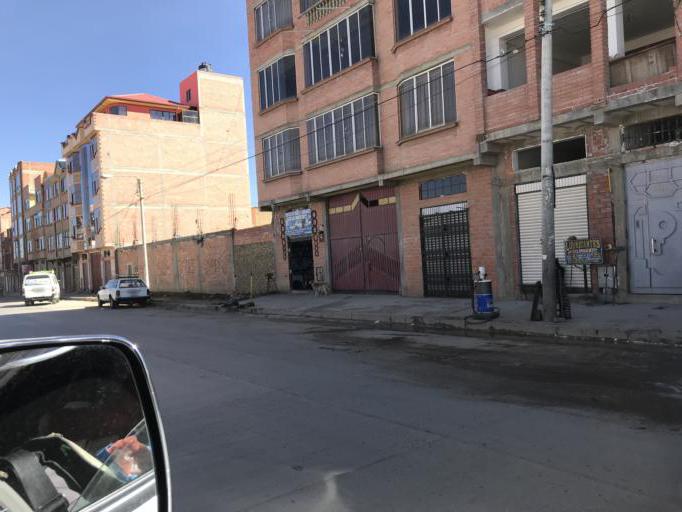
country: BO
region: La Paz
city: La Paz
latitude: -16.4861
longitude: -68.2028
